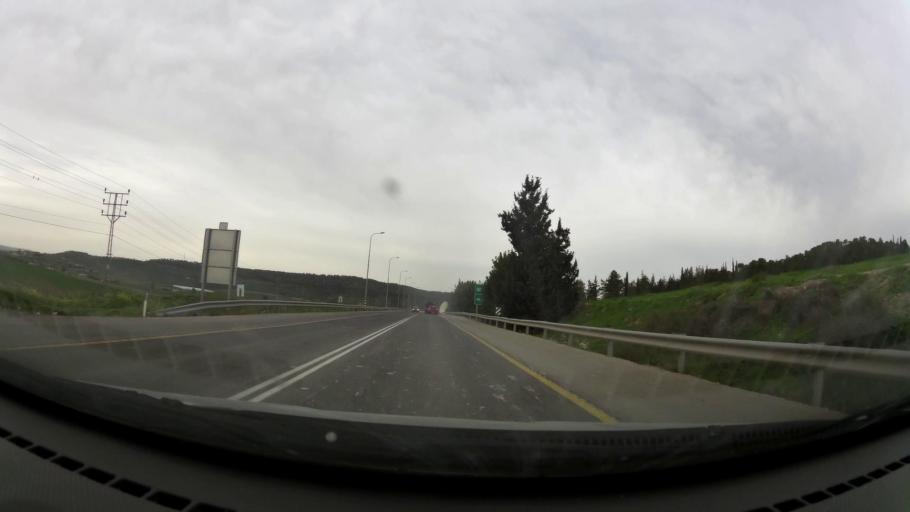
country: IL
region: Jerusalem
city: Bet Shemesh
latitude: 31.6854
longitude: 35.0015
